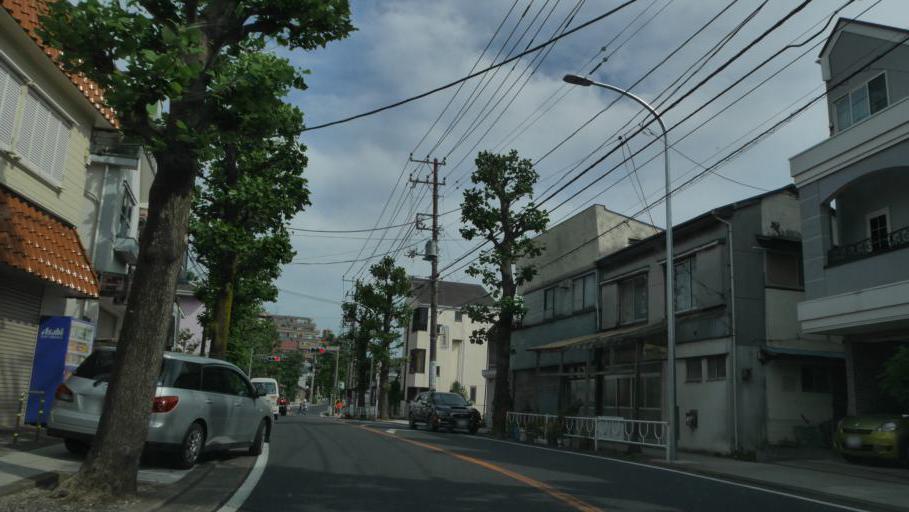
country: JP
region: Kanagawa
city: Yokohama
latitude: 35.4287
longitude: 139.6384
